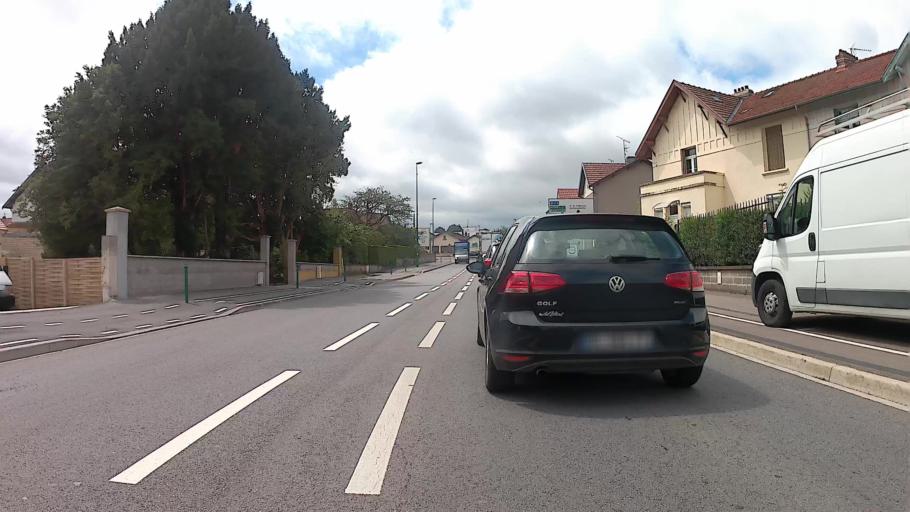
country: FR
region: Lorraine
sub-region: Departement de la Meuse
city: Verdun
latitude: 49.1536
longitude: 5.3966
